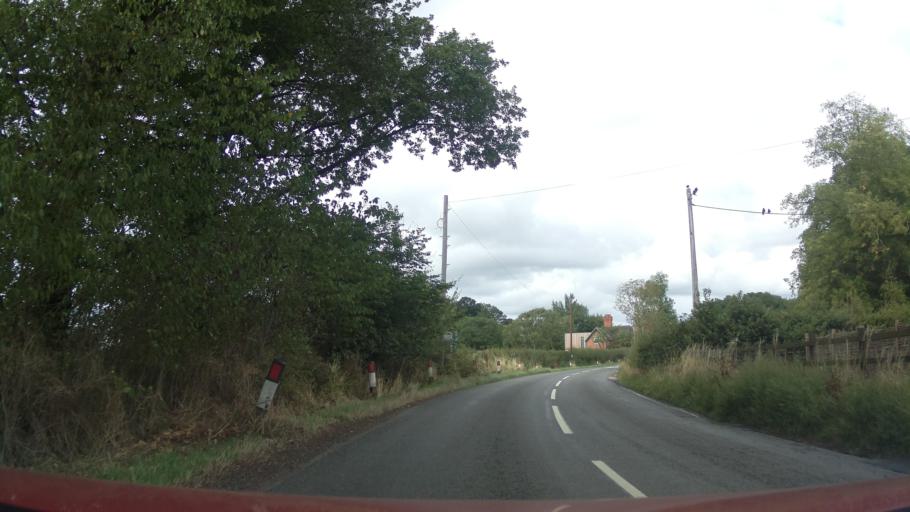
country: GB
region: England
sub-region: Nottinghamshire
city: East Leake
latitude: 52.8076
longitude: -1.1882
